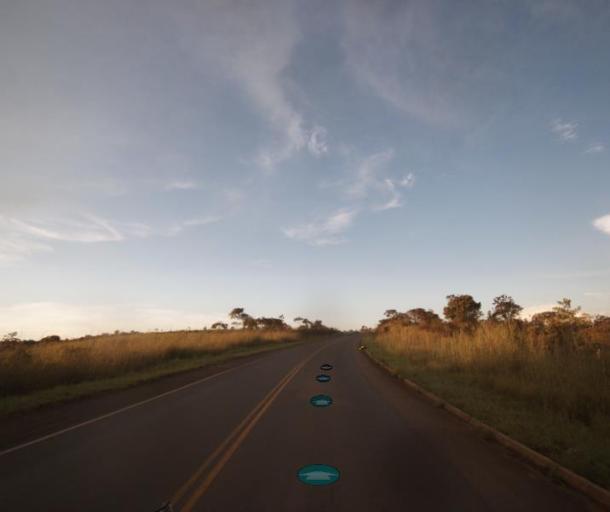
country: BR
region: Goias
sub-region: Abadiania
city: Abadiania
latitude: -16.0839
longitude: -48.8533
